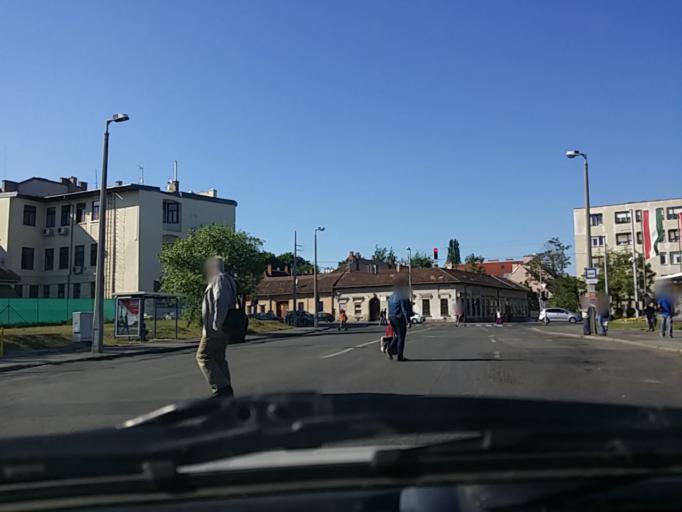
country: HU
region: Budapest
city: Budapest IV. keruelet
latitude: 47.5601
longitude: 19.0827
